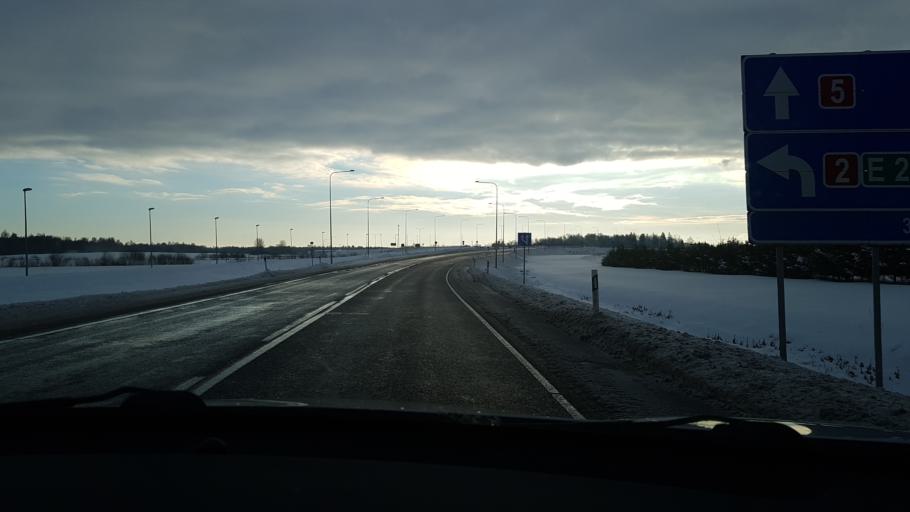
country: EE
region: Jaervamaa
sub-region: Paide linn
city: Paide
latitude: 58.9218
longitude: 25.6245
